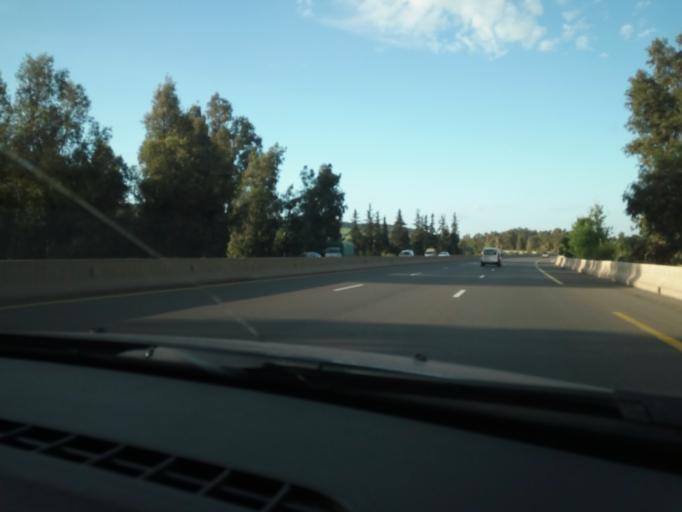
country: DZ
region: Tipaza
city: El Affroun
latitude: 36.4392
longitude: 2.5788
